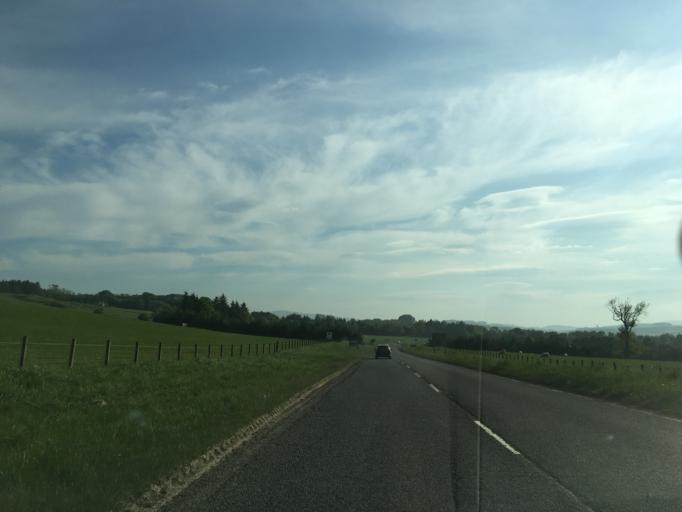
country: GB
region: Scotland
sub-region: The Scottish Borders
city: West Linton
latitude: 55.7302
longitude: -3.3159
